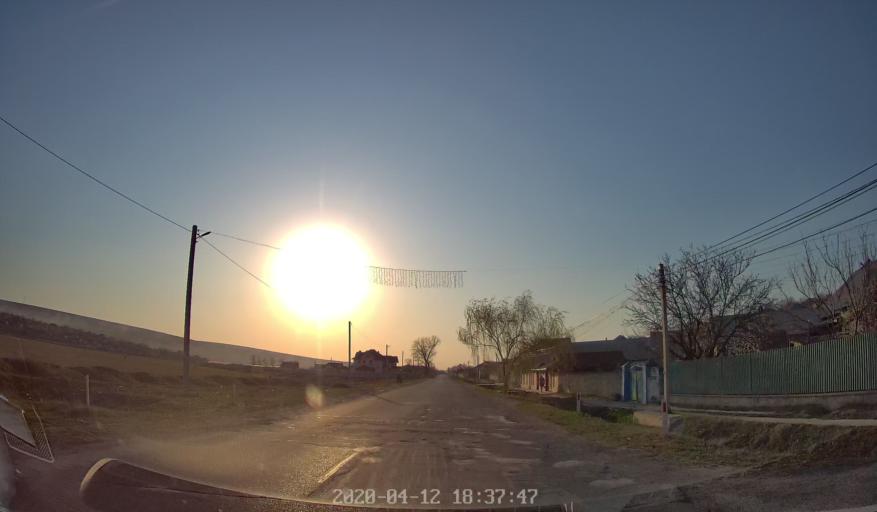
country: MD
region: Chisinau
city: Vadul lui Voda
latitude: 47.1225
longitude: 29.0099
